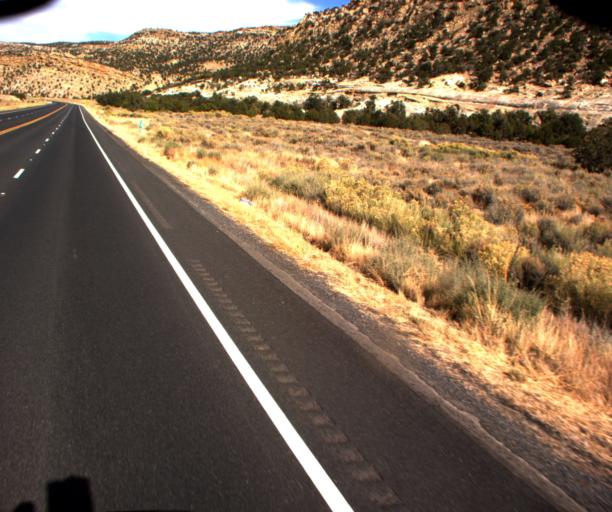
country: US
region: Arizona
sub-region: Navajo County
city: Kayenta
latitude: 36.5740
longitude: -110.4772
